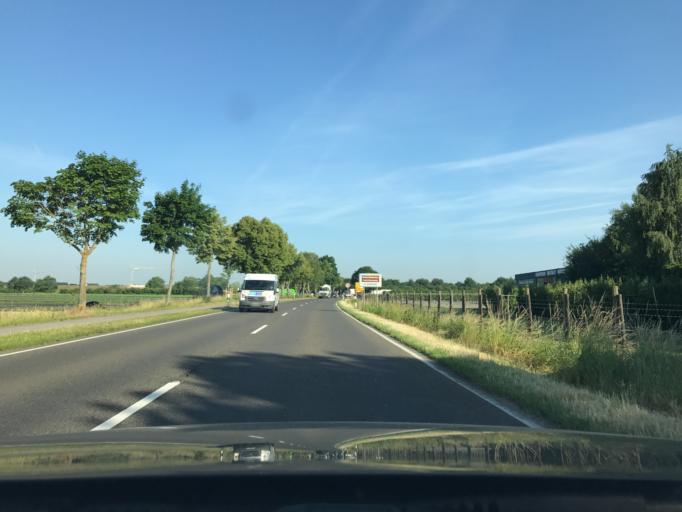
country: DE
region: North Rhine-Westphalia
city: Kempen
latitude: 51.3535
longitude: 6.4411
